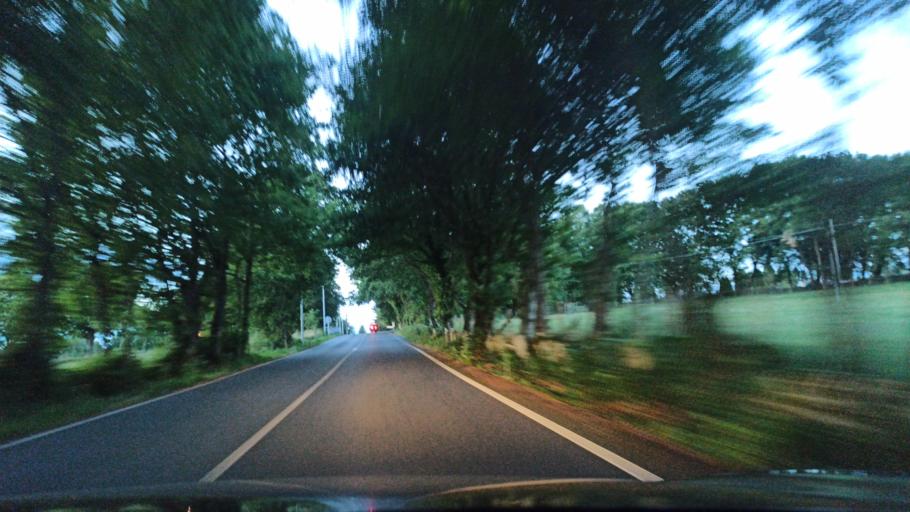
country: ES
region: Galicia
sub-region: Provincia de Lugo
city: Lugo
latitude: 42.9842
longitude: -7.5831
